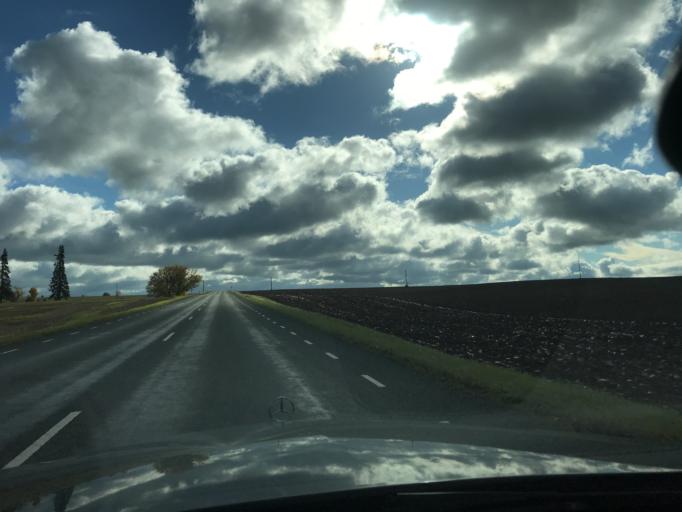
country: EE
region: Vorumaa
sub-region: Antsla vald
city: Vana-Antsla
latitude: 57.9211
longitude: 26.3462
